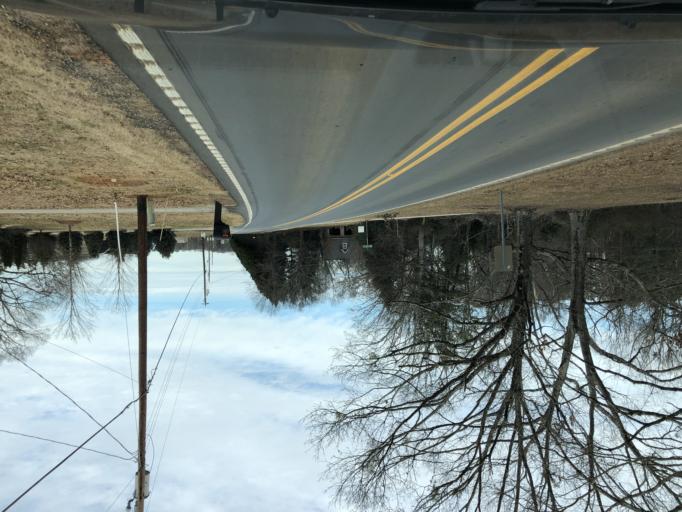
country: US
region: South Carolina
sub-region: Greenville County
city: Five Forks
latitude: 34.8632
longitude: -82.1991
